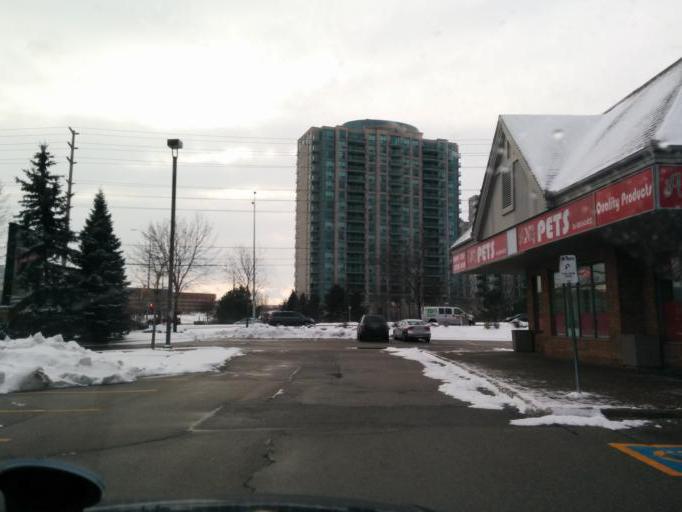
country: CA
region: Ontario
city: Mississauga
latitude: 43.5626
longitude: -79.7105
